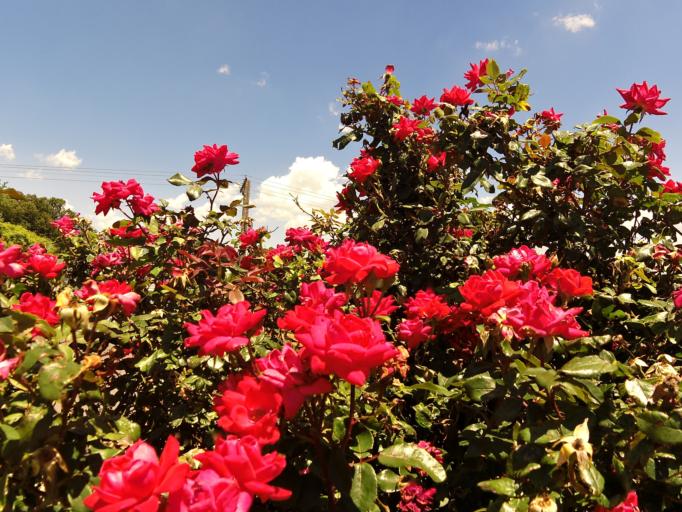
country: US
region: Missouri
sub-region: New Madrid County
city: New Madrid
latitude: 36.5835
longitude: -89.5302
